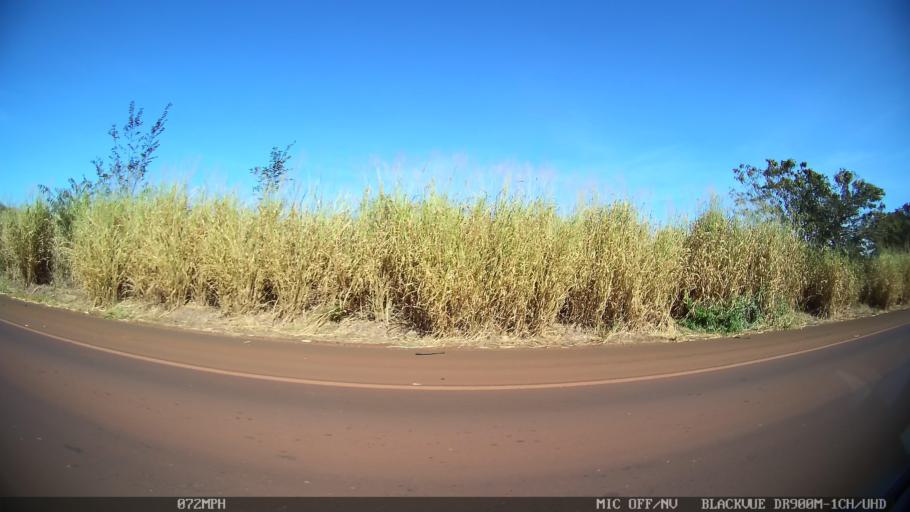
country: BR
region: Sao Paulo
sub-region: Guaira
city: Guaira
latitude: -20.4435
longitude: -48.3248
